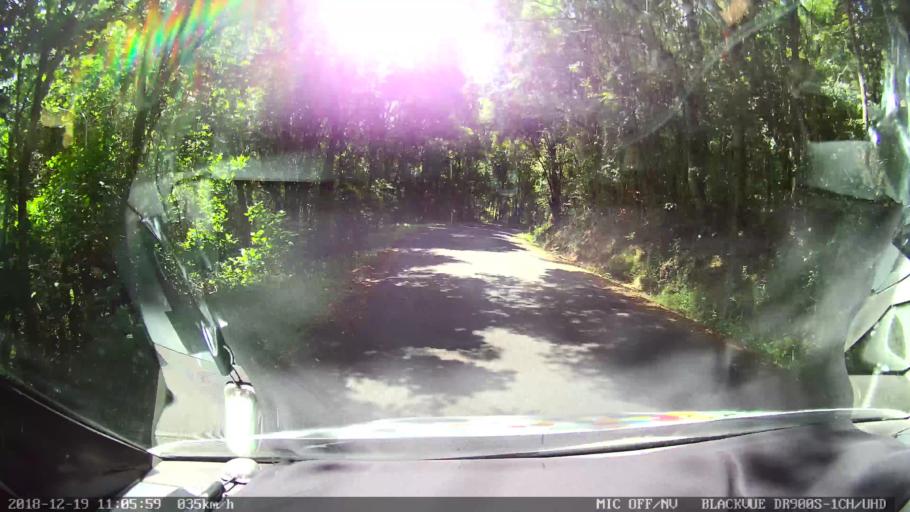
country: AU
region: New South Wales
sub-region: Lismore Municipality
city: Nimbin
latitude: -28.6204
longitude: 153.2654
